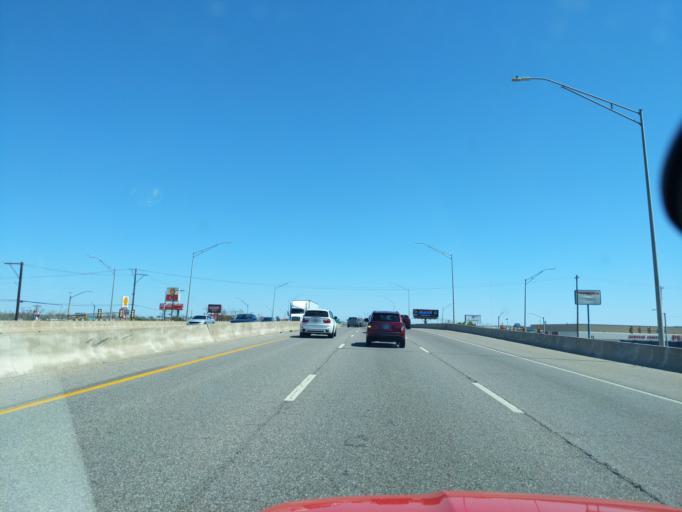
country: US
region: Oklahoma
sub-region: Cleveland County
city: Moore
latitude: 35.3913
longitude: -97.5223
